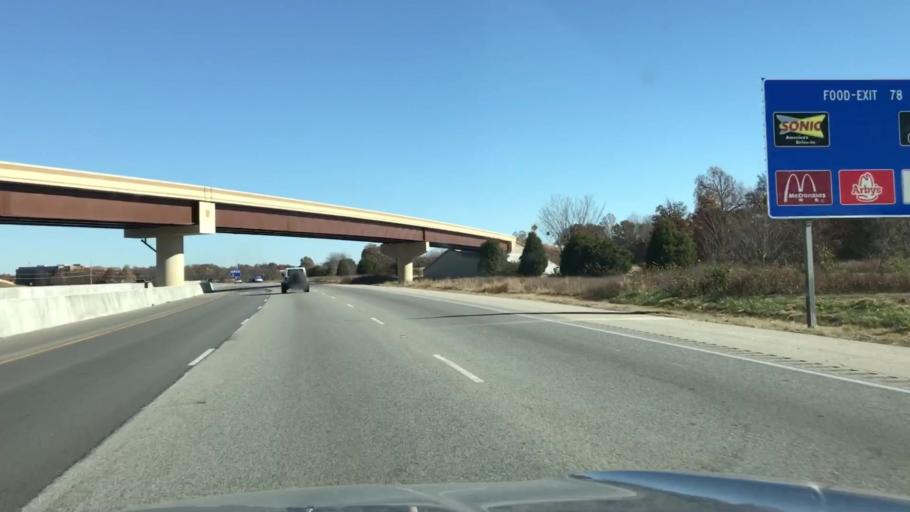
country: US
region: Arkansas
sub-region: Benton County
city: Lowell
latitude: 36.2380
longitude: -94.1592
